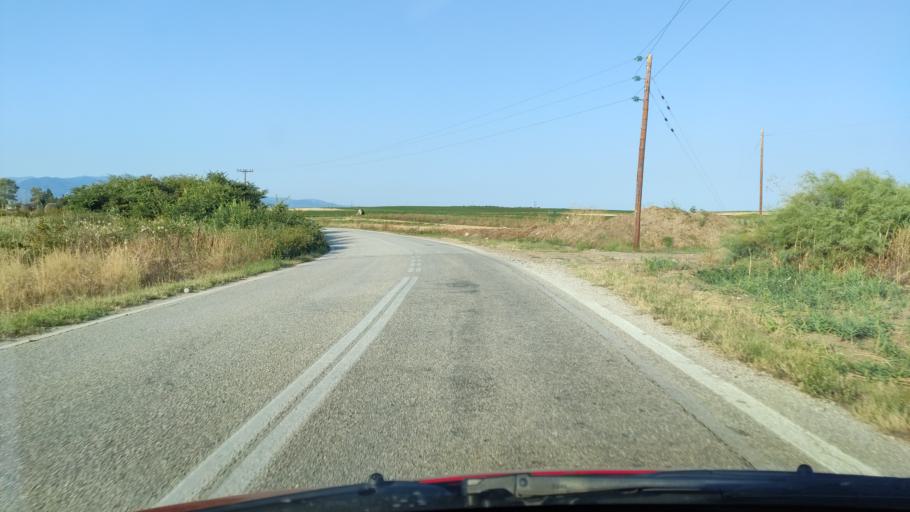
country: GR
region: East Macedonia and Thrace
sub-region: Nomos Rodopis
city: Iasmos
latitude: 41.0002
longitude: 25.1739
